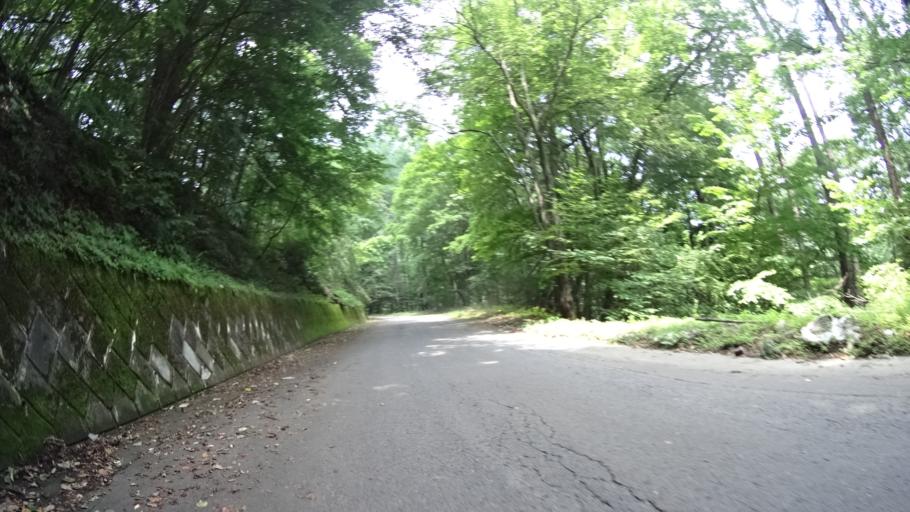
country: JP
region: Nagano
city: Saku
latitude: 36.0908
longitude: 138.6925
